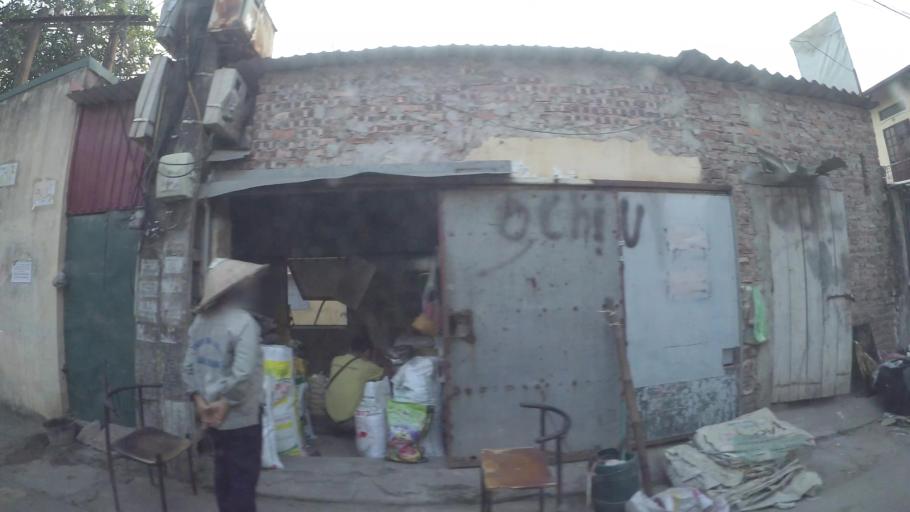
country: VN
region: Ha Noi
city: Van Dien
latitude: 20.9303
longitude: 105.8356
